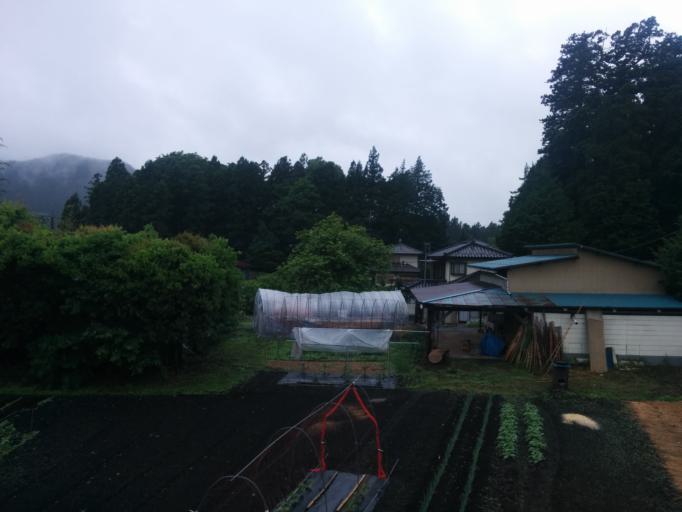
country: JP
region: Tochigi
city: Imaichi
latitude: 36.6433
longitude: 139.7258
